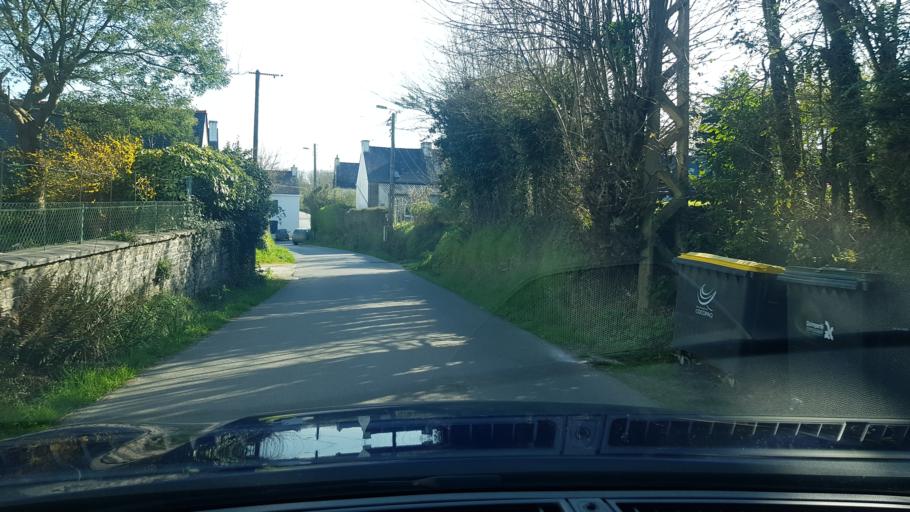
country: FR
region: Brittany
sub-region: Departement du Finistere
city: Moelan-sur-Mer
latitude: 47.7821
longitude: -3.6283
